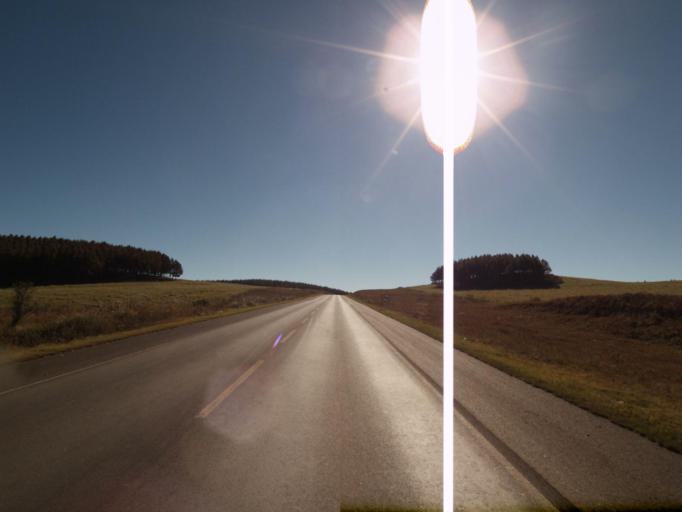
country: BR
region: Parana
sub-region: Palmas
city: Palmas
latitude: -26.7514
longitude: -51.6627
